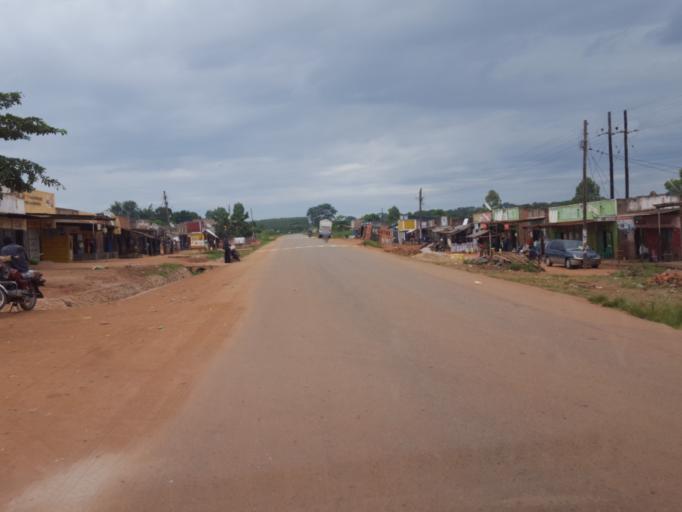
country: UG
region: Central Region
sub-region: Kiboga District
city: Kiboga
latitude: 1.0673
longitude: 31.6532
